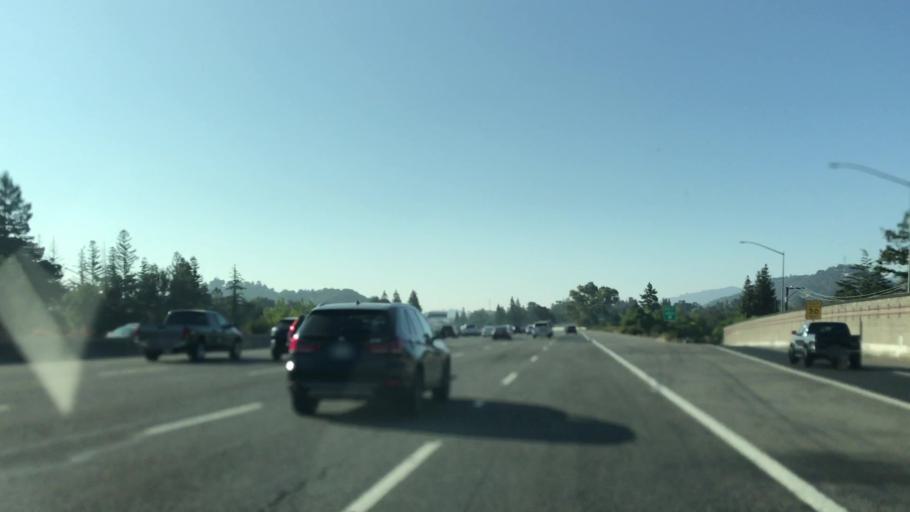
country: US
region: California
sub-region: Contra Costa County
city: Saranap
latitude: 37.8882
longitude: -122.0573
